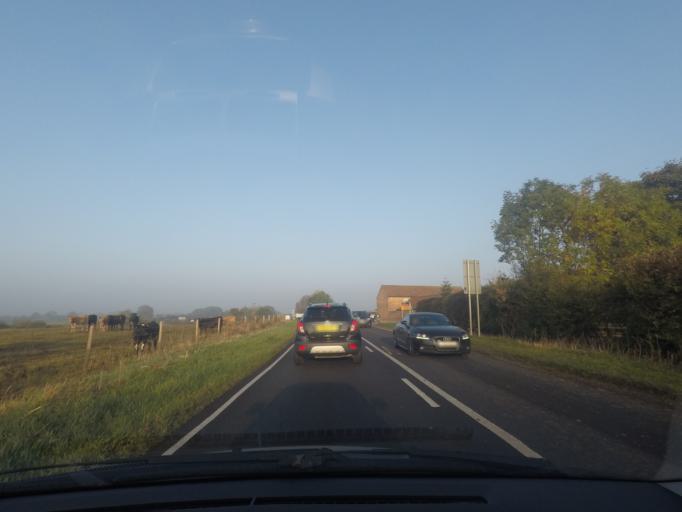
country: GB
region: England
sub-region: City and Borough of Leeds
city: Walton
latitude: 53.9973
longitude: -1.2579
